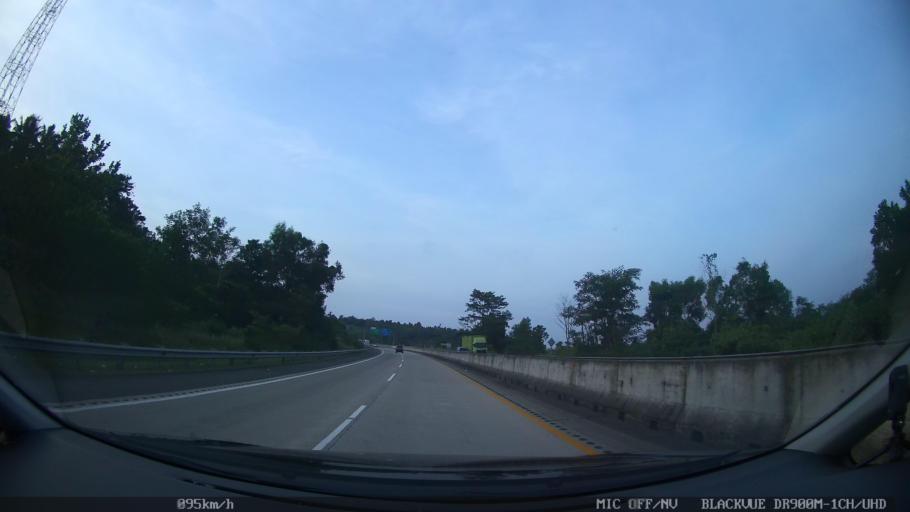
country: ID
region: Lampung
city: Penengahan
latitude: -5.8205
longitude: 105.7367
